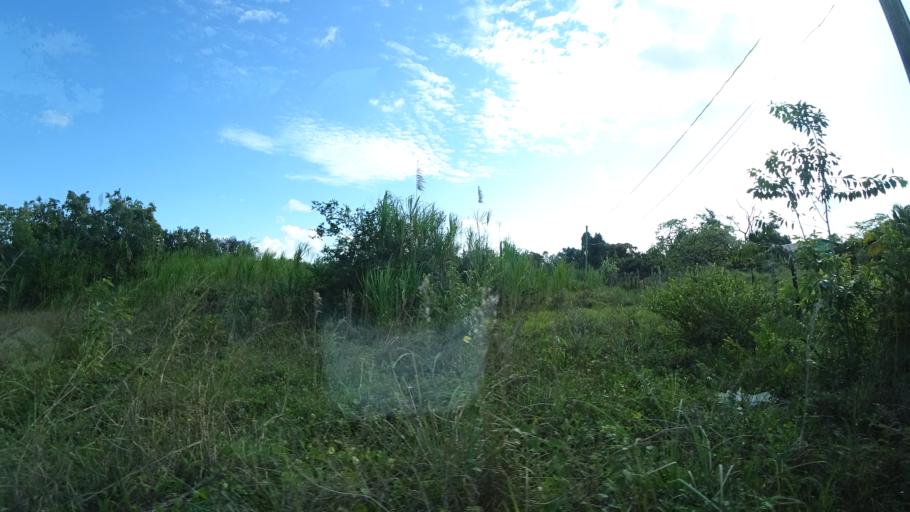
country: BZ
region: Belize
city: Belize City
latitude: 17.5566
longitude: -88.4055
